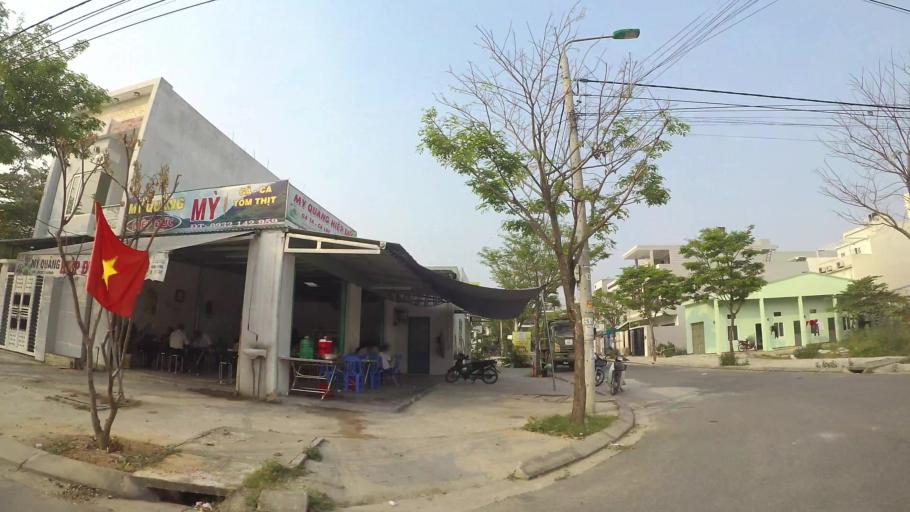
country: VN
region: Da Nang
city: Cam Le
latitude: 16.0096
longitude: 108.2209
